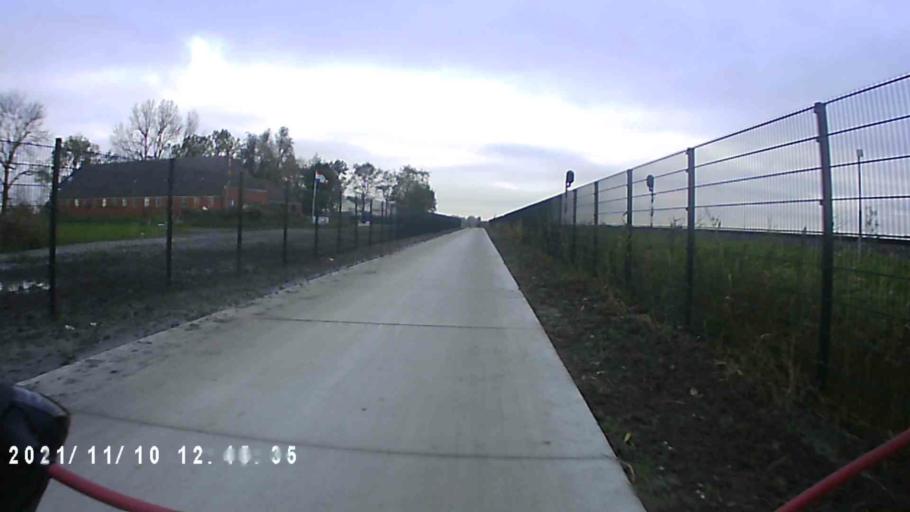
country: NL
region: Groningen
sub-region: Gemeente Groningen
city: Korrewegwijk
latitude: 53.2616
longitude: 6.5473
